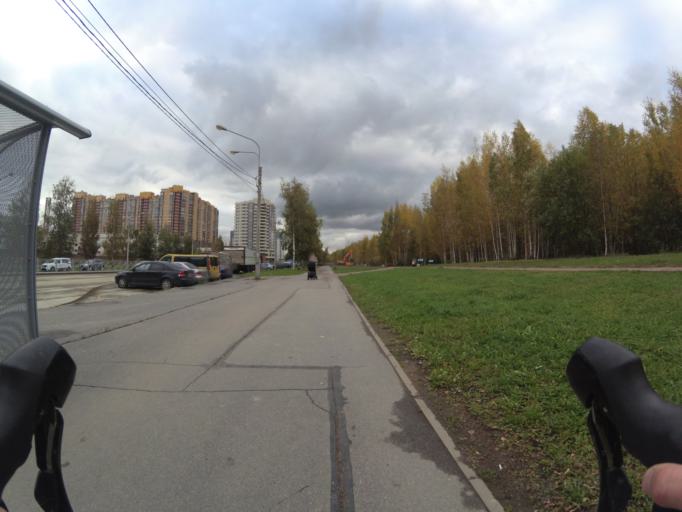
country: RU
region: Leningrad
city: Untolovo
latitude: 60.0025
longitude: 30.1946
